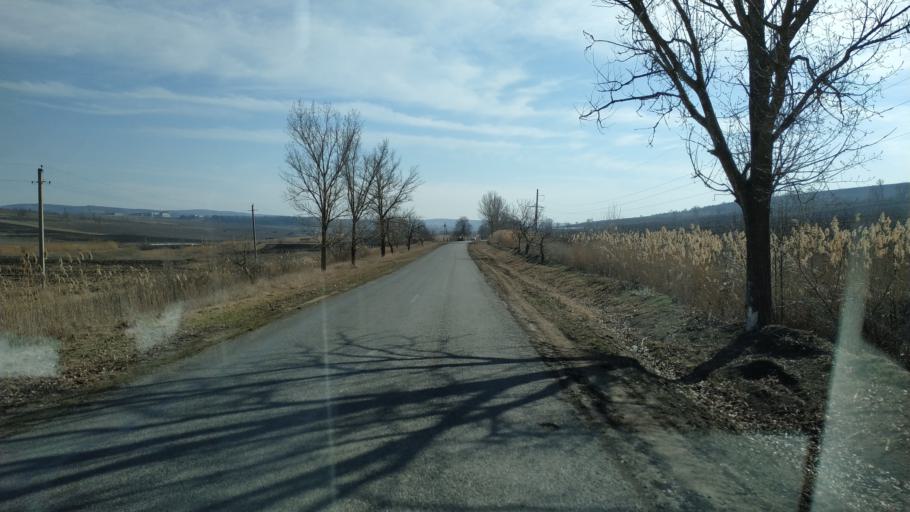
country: MD
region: Nisporeni
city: Nisporeni
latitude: 47.0954
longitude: 28.1332
